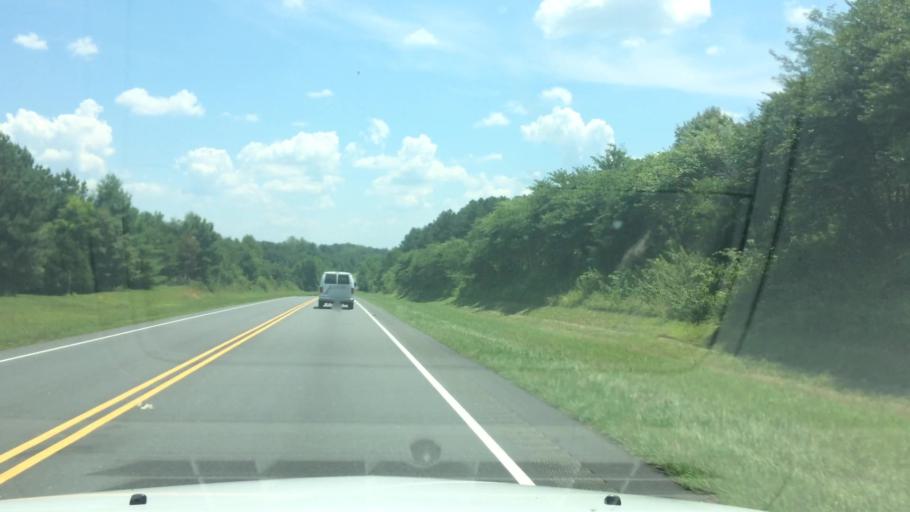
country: US
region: North Carolina
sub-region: Alexander County
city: Stony Point
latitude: 35.8494
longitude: -81.0356
